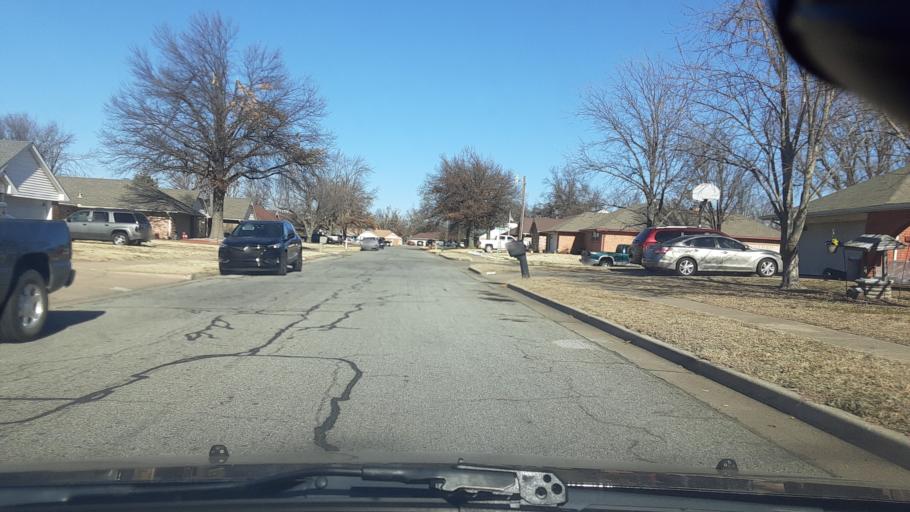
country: US
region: Oklahoma
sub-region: Kay County
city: Ponca City
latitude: 36.7290
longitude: -97.0891
